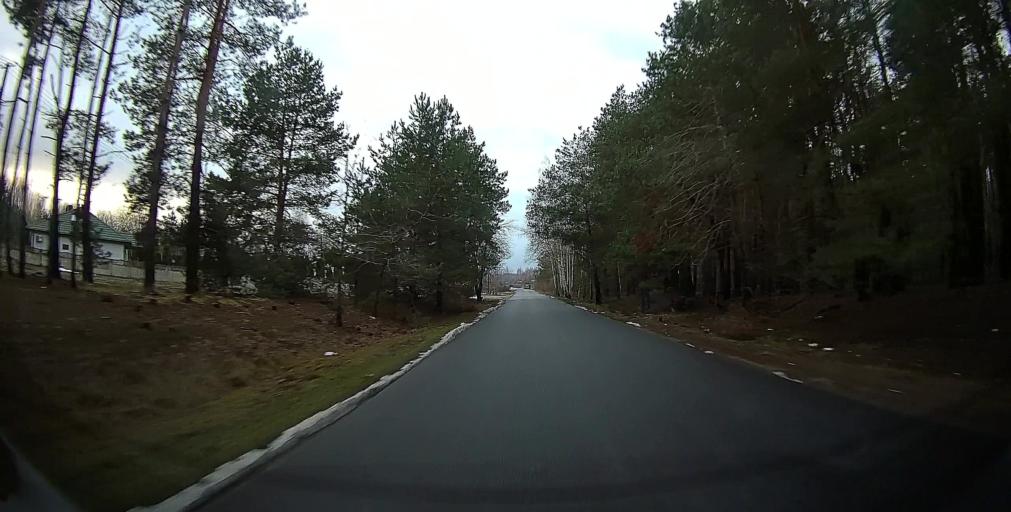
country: PL
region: Masovian Voivodeship
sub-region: Radom
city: Radom
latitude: 51.4532
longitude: 21.1285
